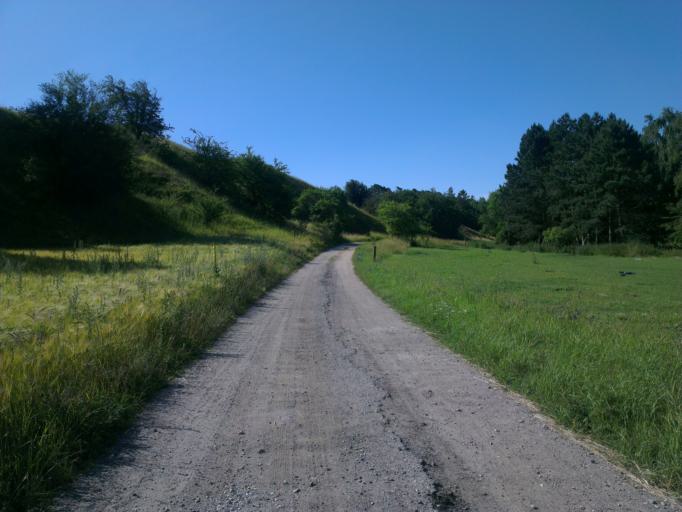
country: DK
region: Capital Region
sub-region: Frederikssund Kommune
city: Frederikssund
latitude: 55.7866
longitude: 12.0381
